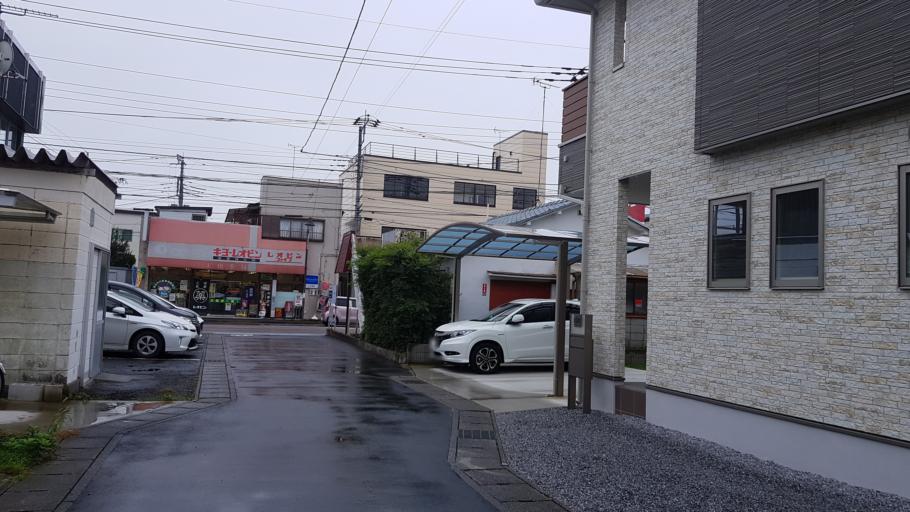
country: JP
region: Tochigi
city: Utsunomiya-shi
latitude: 36.5712
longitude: 139.9188
